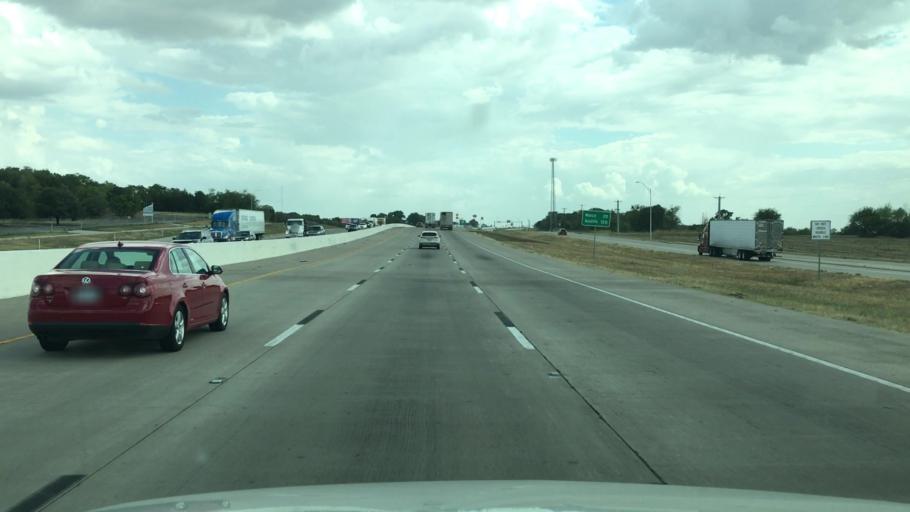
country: US
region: Texas
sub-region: McLennan County
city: West
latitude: 31.8154
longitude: -97.0985
